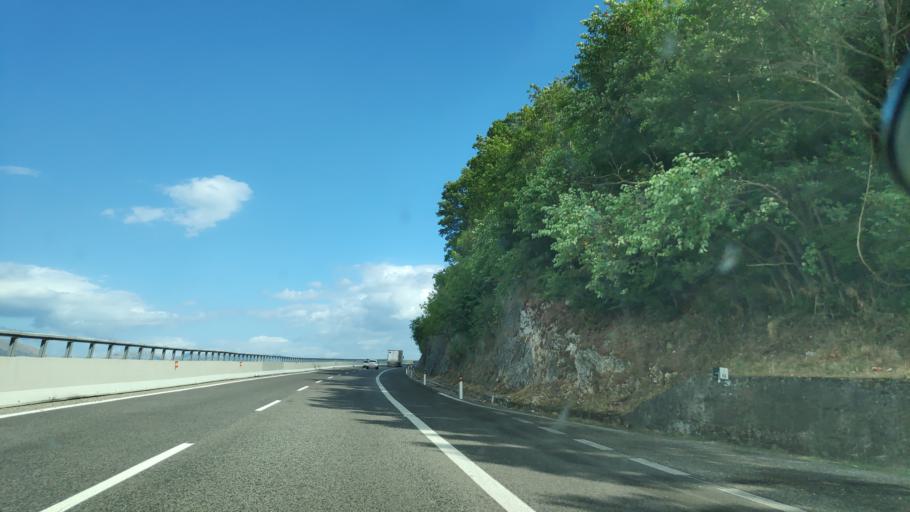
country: IT
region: Campania
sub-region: Provincia di Salerno
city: Sicignano degli Alburni
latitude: 40.5904
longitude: 15.3309
